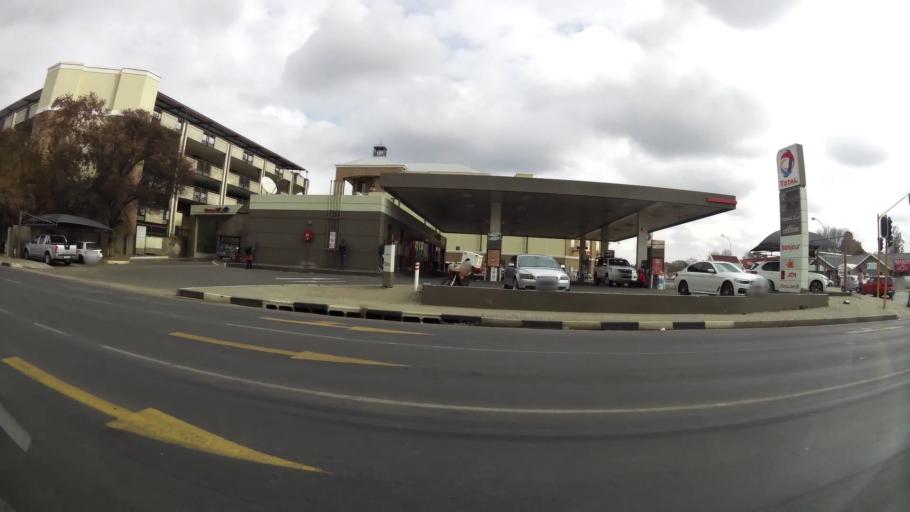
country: ZA
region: Orange Free State
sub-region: Mangaung Metropolitan Municipality
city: Bloemfontein
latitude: -29.1083
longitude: 26.2026
